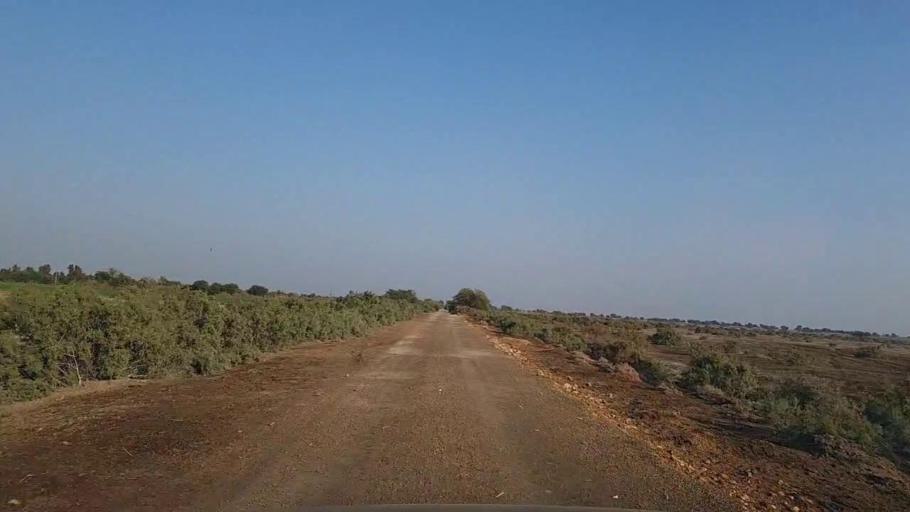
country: PK
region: Sindh
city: Tando Mittha Khan
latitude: 25.9251
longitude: 69.0908
